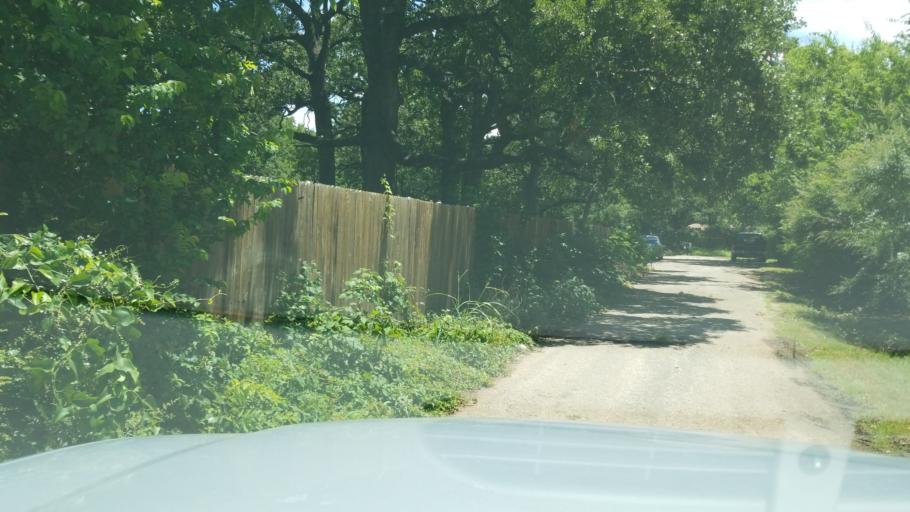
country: US
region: Texas
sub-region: Dallas County
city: Irving
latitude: 32.8057
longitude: -96.9138
